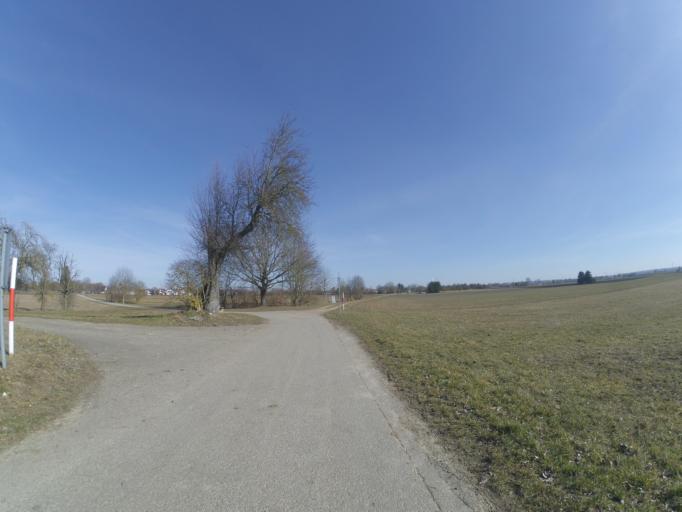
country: DE
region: Baden-Wuerttemberg
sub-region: Regierungsbezirk Stuttgart
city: Sontheim an der Brenz
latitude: 48.5473
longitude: 10.2831
